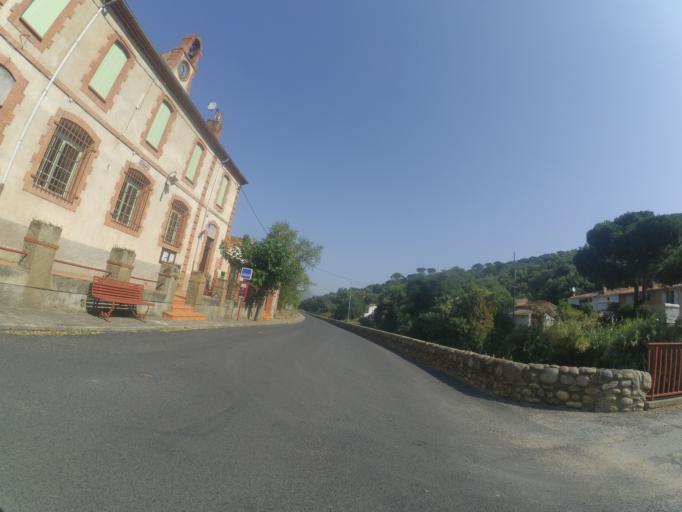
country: FR
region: Languedoc-Roussillon
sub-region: Departement des Pyrenees-Orientales
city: Ille-sur-Tet
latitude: 42.6479
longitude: 2.6252
